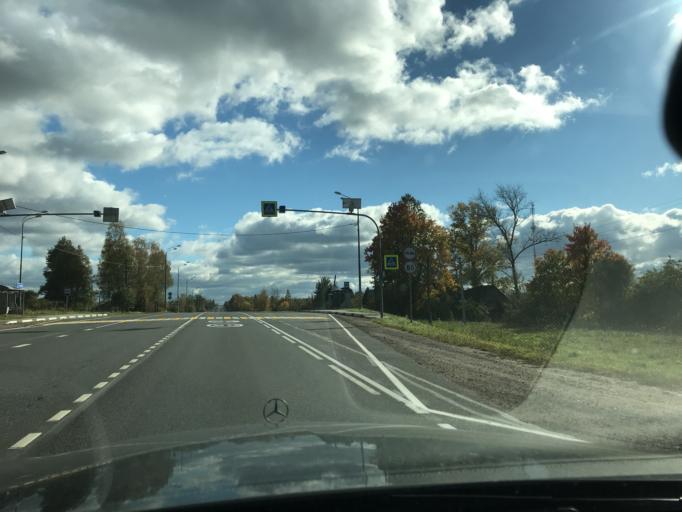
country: RU
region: Pskov
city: Ostrov
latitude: 57.1315
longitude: 28.5186
